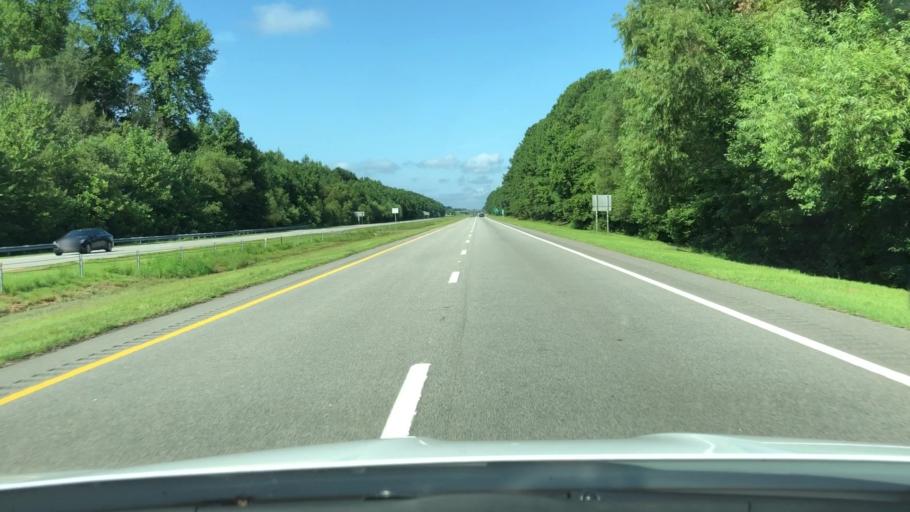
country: US
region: North Carolina
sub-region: Chowan County
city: Edenton
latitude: 36.0652
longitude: -76.6504
